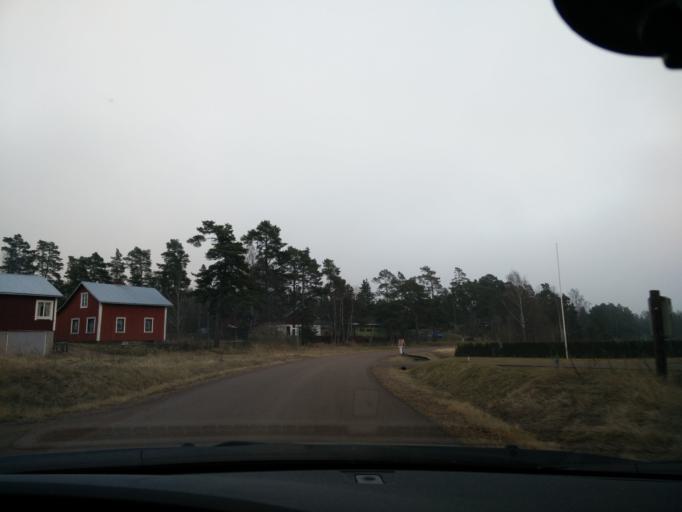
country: AX
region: Mariehamns stad
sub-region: Mariehamn
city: Mariehamn
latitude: 60.1299
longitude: 19.9182
